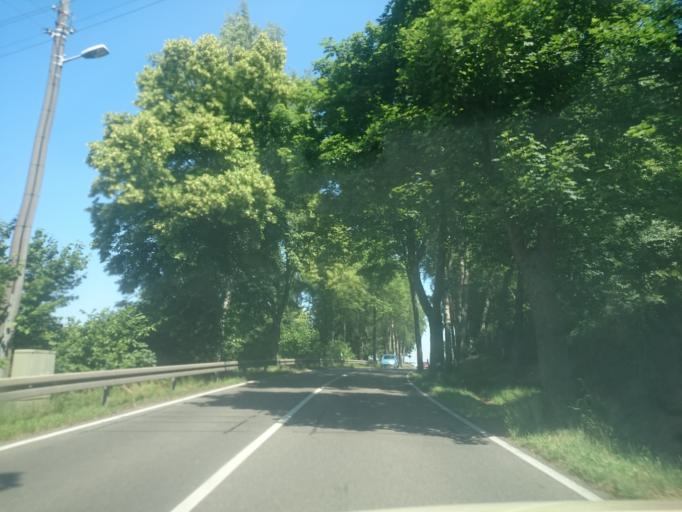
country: DE
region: Saxony
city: Freiberg
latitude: 50.8915
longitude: 13.3307
